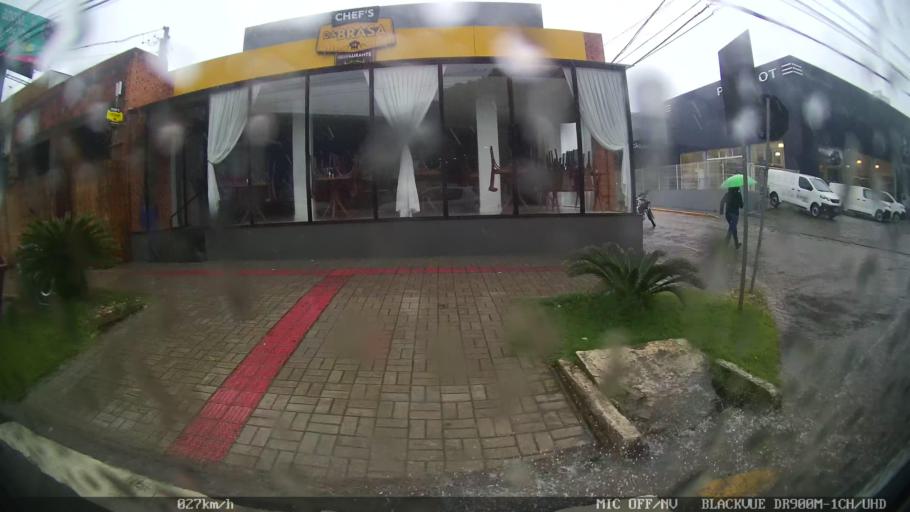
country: BR
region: Santa Catarina
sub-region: Balneario Camboriu
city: Balneario Camboriu
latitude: -26.9522
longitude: -48.6406
